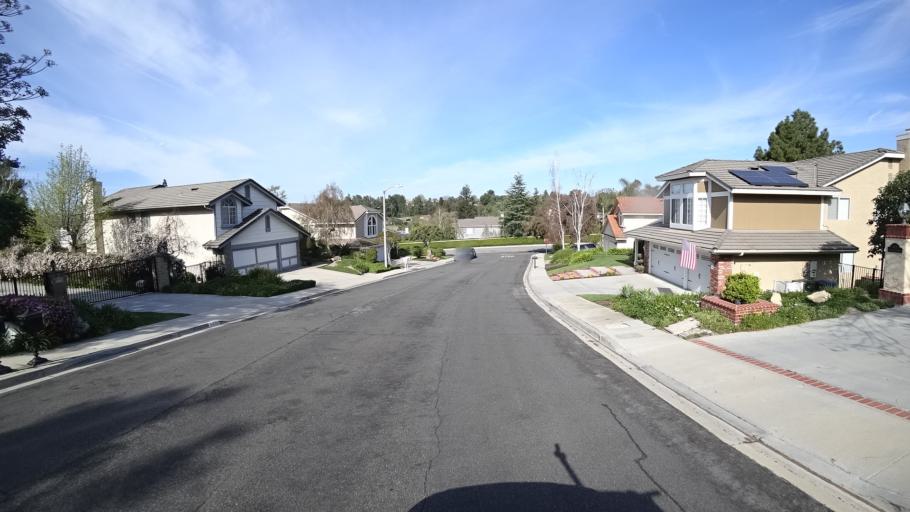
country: US
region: California
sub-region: Ventura County
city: Thousand Oaks
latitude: 34.2169
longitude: -118.8332
